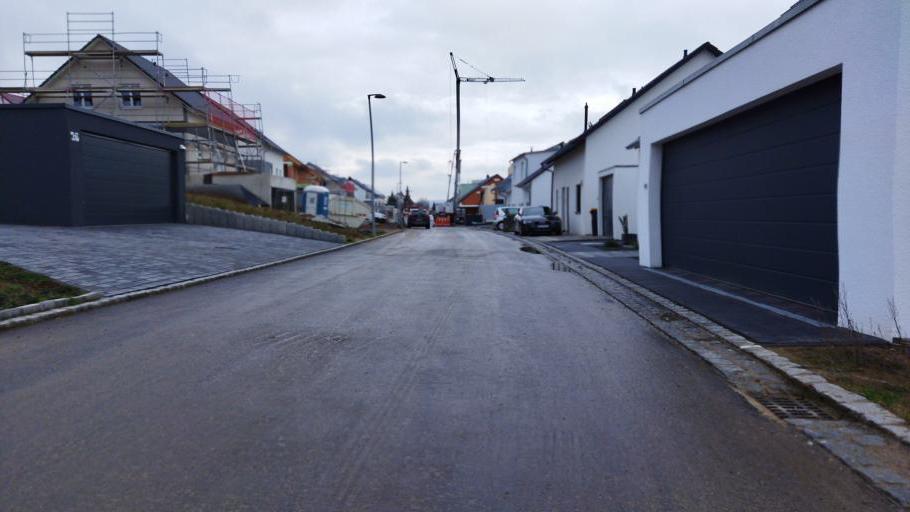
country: DE
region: Baden-Wuerttemberg
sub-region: Regierungsbezirk Stuttgart
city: Neckarsulm
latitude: 49.1684
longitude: 9.1856
